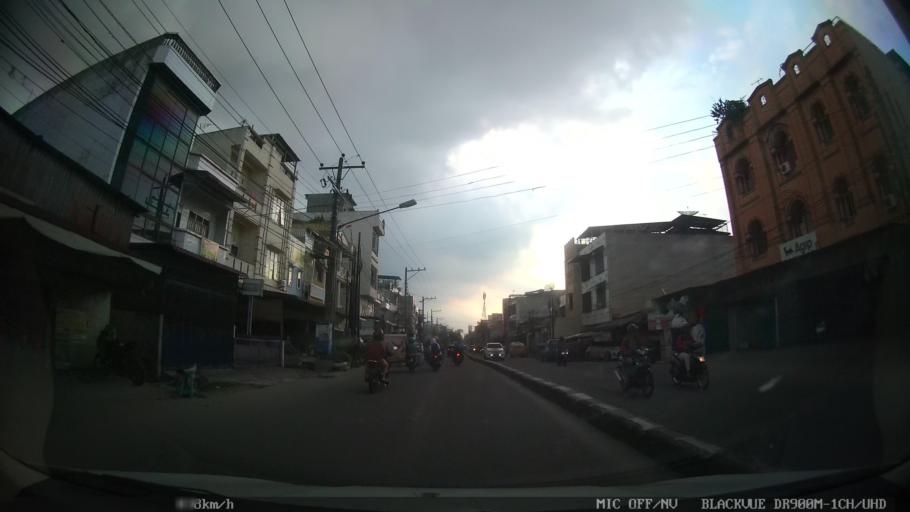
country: ID
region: North Sumatra
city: Medan
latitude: 3.5821
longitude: 98.7079
